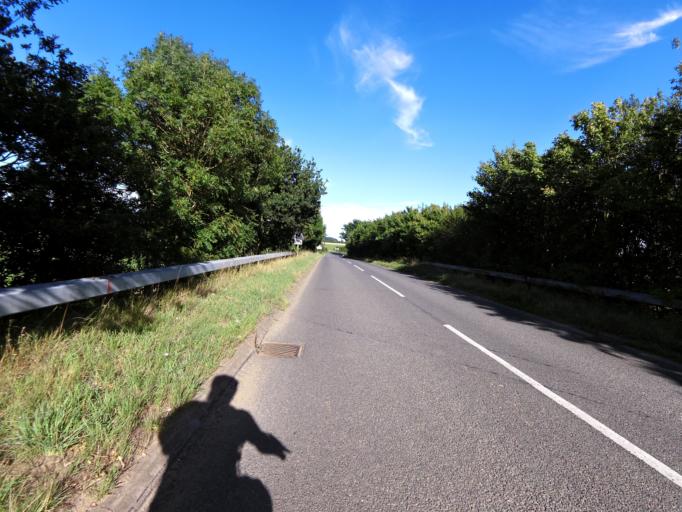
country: GB
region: England
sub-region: Suffolk
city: Kesgrave
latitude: 52.0349
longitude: 1.2591
